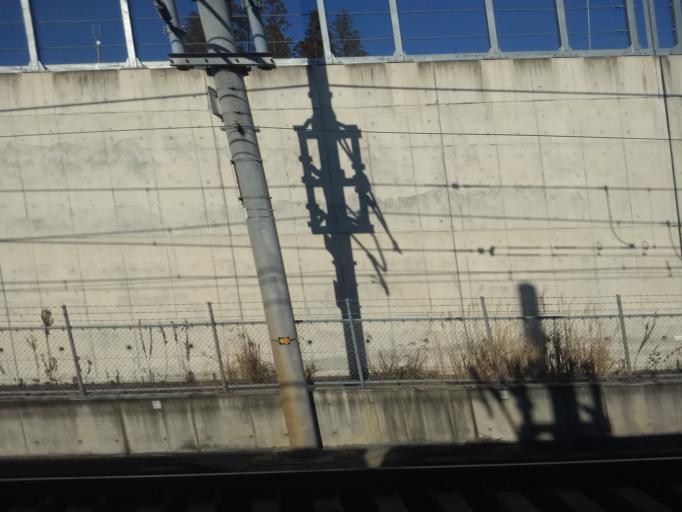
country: JP
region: Chiba
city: Sakura
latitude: 35.7857
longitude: 140.2108
